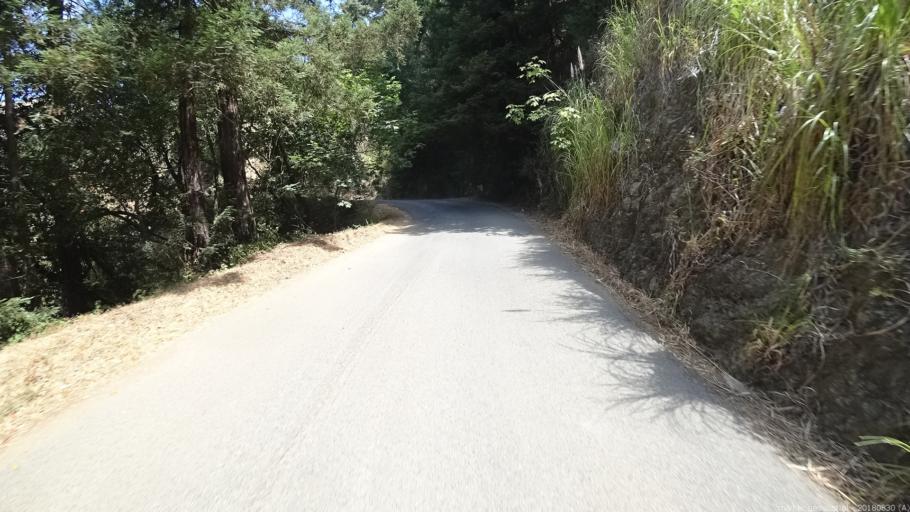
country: US
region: California
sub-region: Monterey County
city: Greenfield
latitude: 35.9945
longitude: -121.4882
